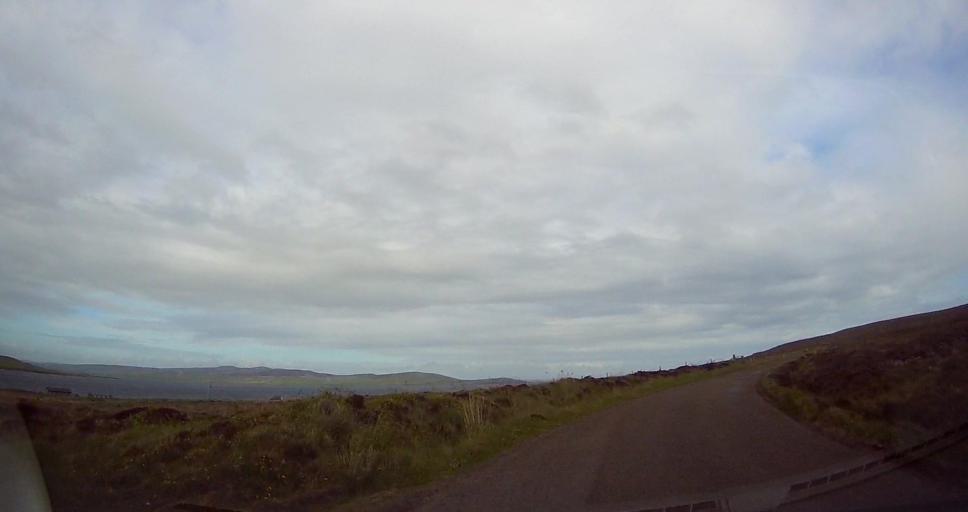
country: GB
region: Scotland
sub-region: Orkney Islands
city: Stromness
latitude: 58.9032
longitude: -3.3022
